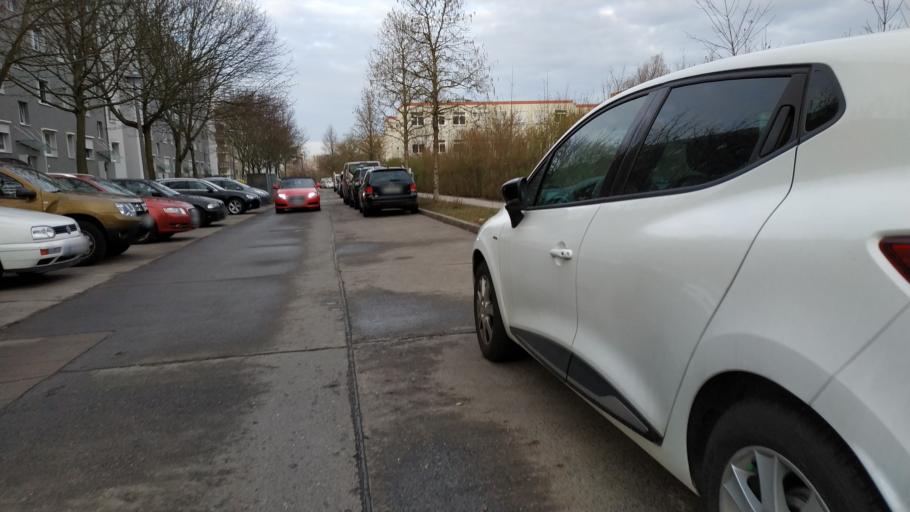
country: DE
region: Berlin
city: Marzahn
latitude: 52.5424
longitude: 13.5884
